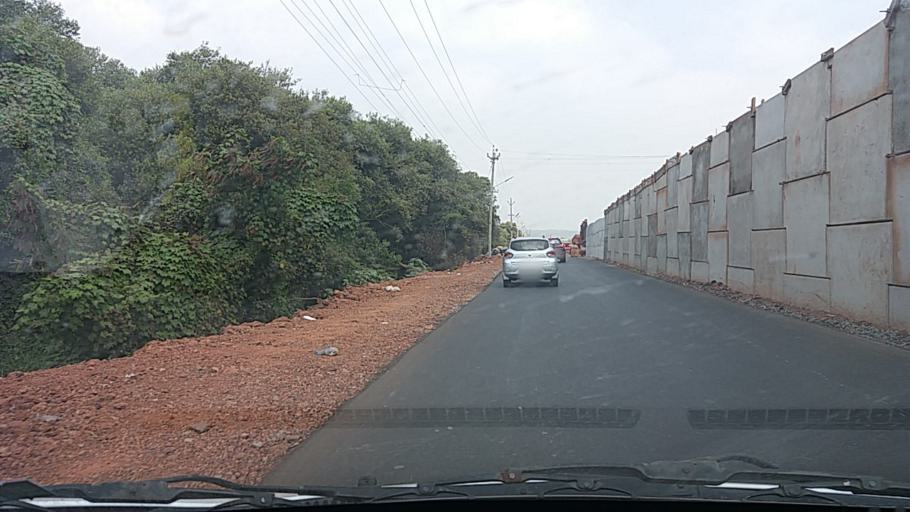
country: IN
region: Goa
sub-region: North Goa
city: Bambolim
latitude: 15.4800
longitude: 73.8480
